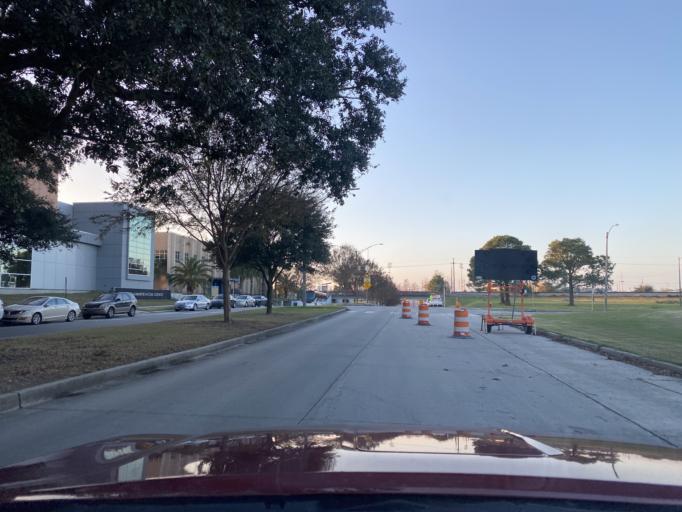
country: US
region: Louisiana
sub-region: Orleans Parish
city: New Orleans
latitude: 30.0269
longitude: -90.0436
